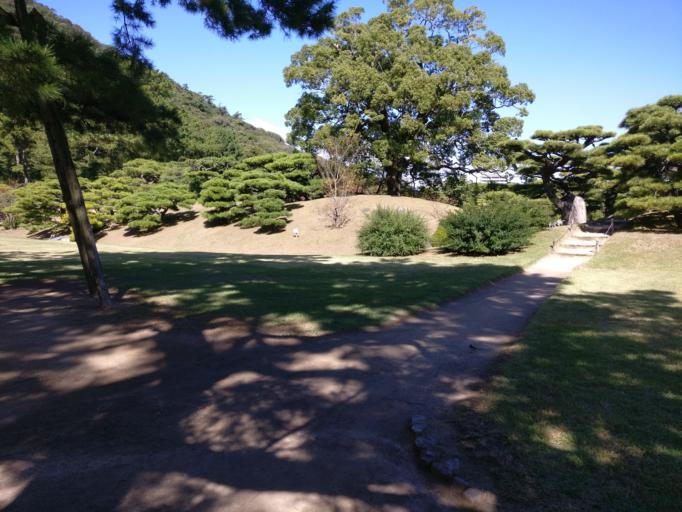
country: JP
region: Kagawa
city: Takamatsu-shi
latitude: 34.3279
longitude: 134.0441
